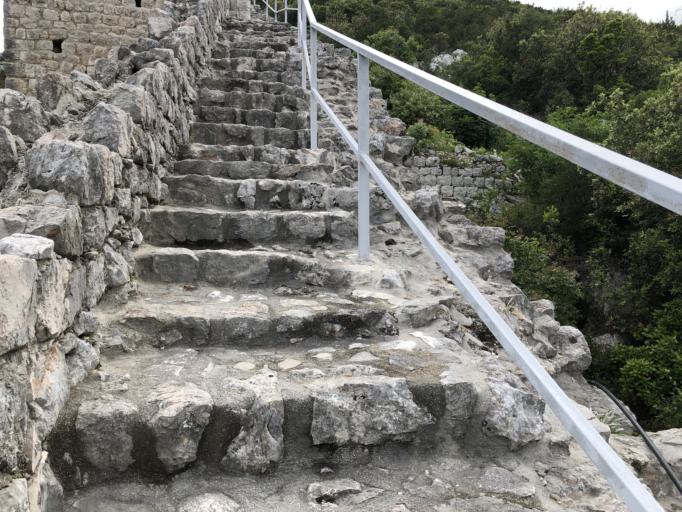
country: HR
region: Dubrovacko-Neretvanska
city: Ston
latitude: 42.8442
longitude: 17.7005
